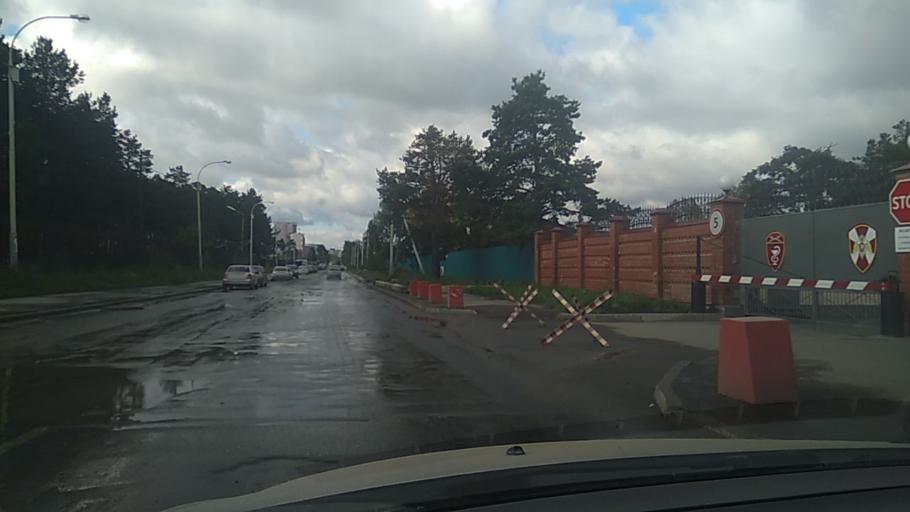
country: RU
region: Sverdlovsk
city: Shirokaya Rechka
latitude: 56.8080
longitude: 60.5064
